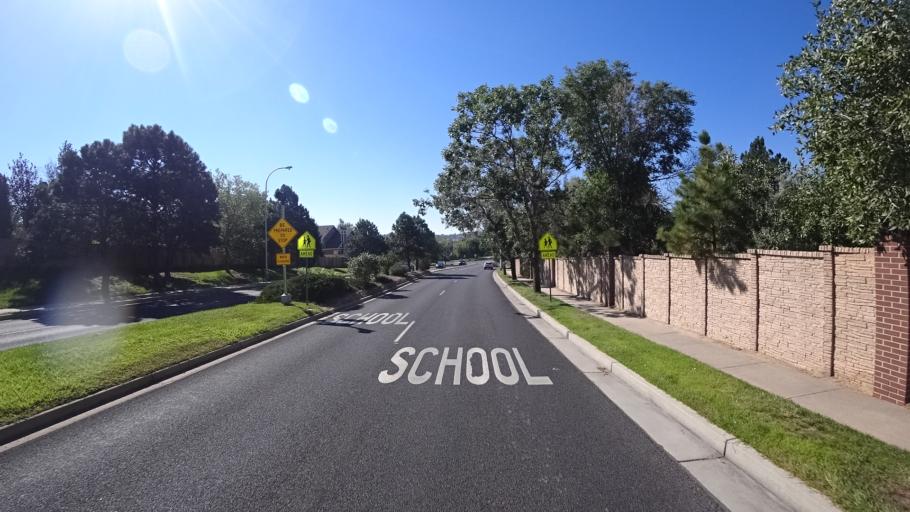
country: US
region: Colorado
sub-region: El Paso County
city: Cimarron Hills
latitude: 38.9340
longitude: -104.7546
